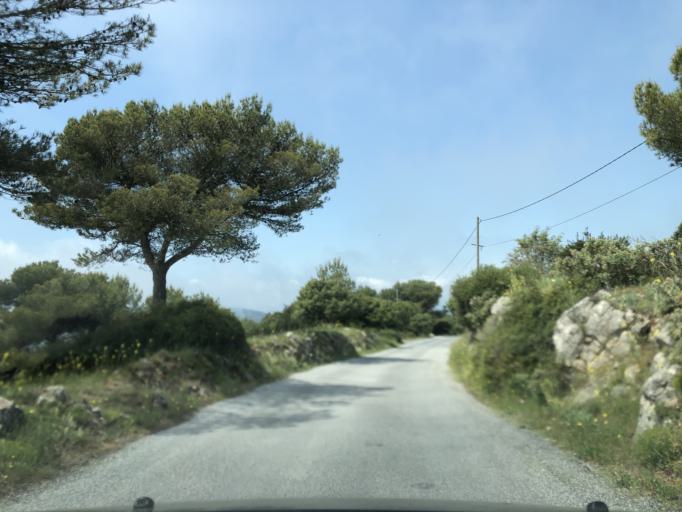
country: FR
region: Provence-Alpes-Cote d'Azur
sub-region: Departement des Alpes-Maritimes
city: Eze
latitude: 43.7395
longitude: 7.3571
